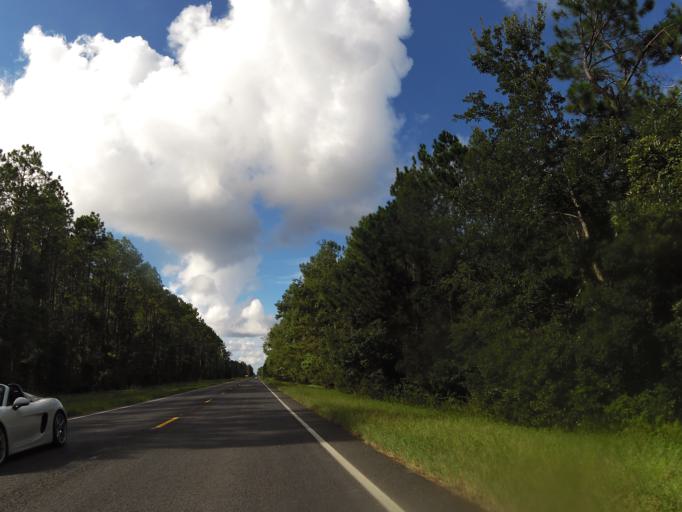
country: US
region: Georgia
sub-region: Camden County
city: Woodbine
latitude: 30.9068
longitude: -81.7112
